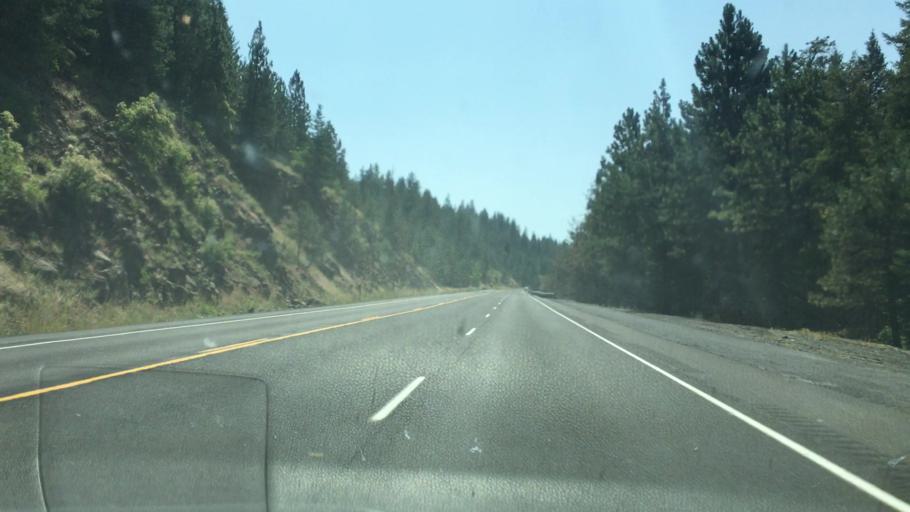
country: US
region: Idaho
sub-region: Idaho County
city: Grangeville
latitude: 45.8601
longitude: -116.2372
